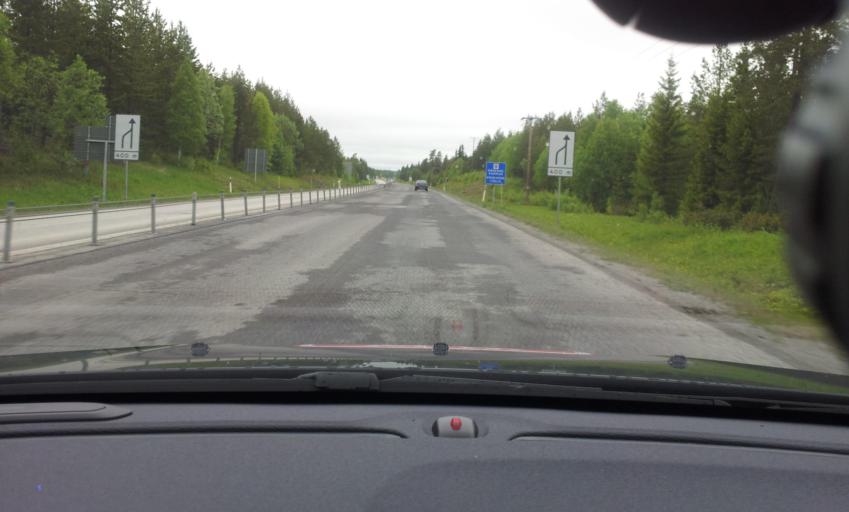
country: SE
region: Jaemtland
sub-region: OEstersunds Kommun
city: Ostersund
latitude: 63.2224
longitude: 14.6261
